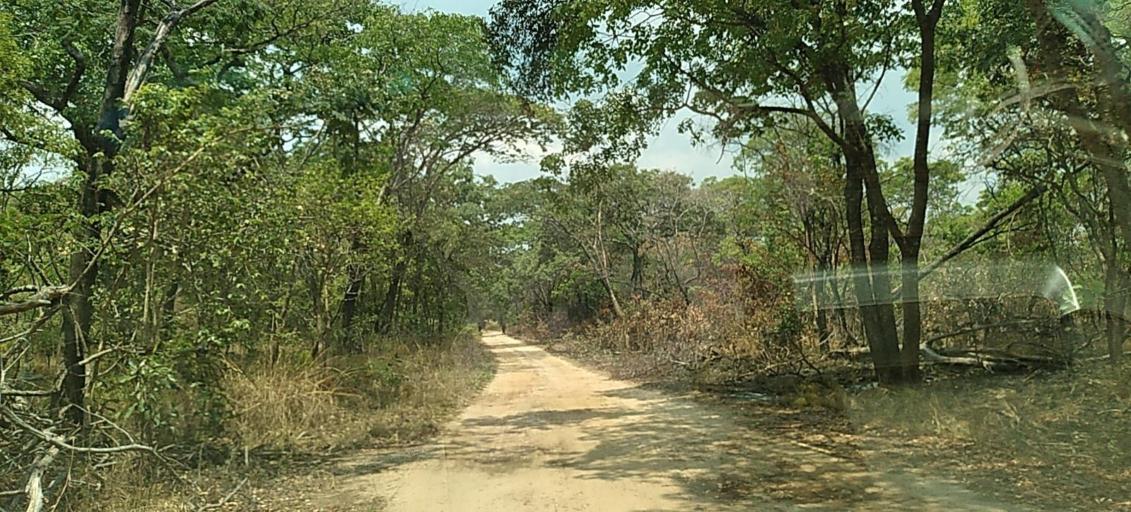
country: ZM
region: Copperbelt
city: Chingola
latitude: -12.7705
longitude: 27.6933
